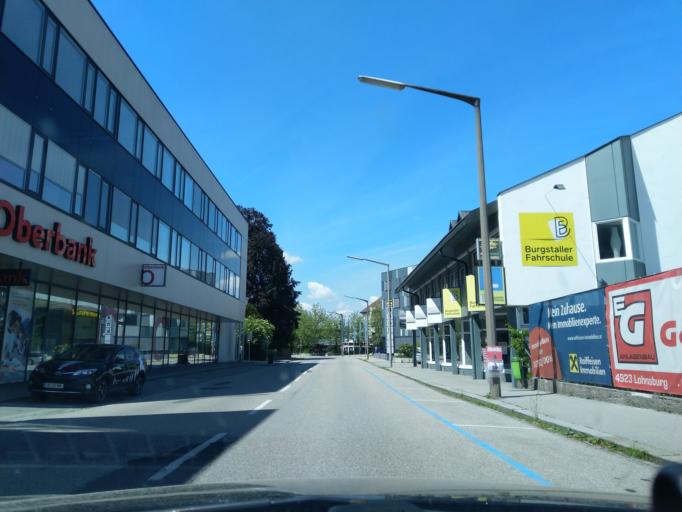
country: AT
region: Upper Austria
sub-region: Politischer Bezirk Ried im Innkreis
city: Ried im Innkreis
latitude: 48.2109
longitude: 13.4853
